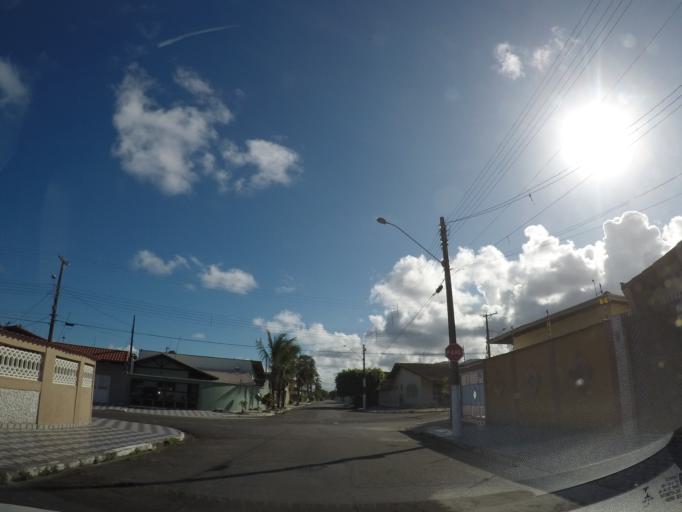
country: BR
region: Sao Paulo
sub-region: Mongagua
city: Mongagua
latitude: -24.0572
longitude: -46.5475
